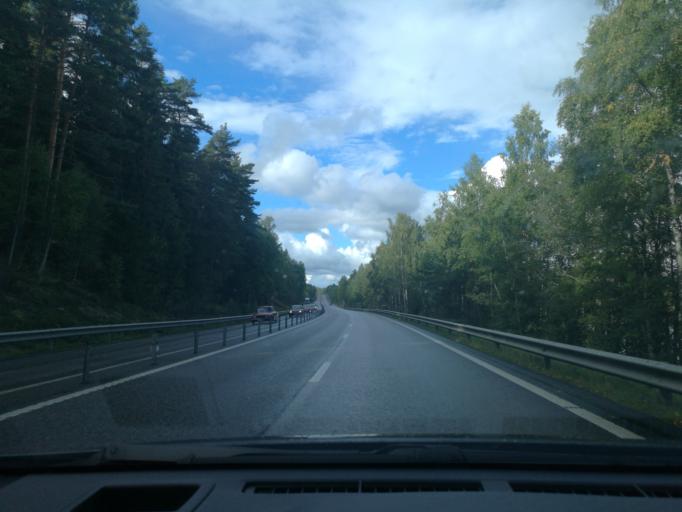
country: SE
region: OEstergoetland
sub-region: Norrkopings Kommun
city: Jursla
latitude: 58.7519
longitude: 16.1766
